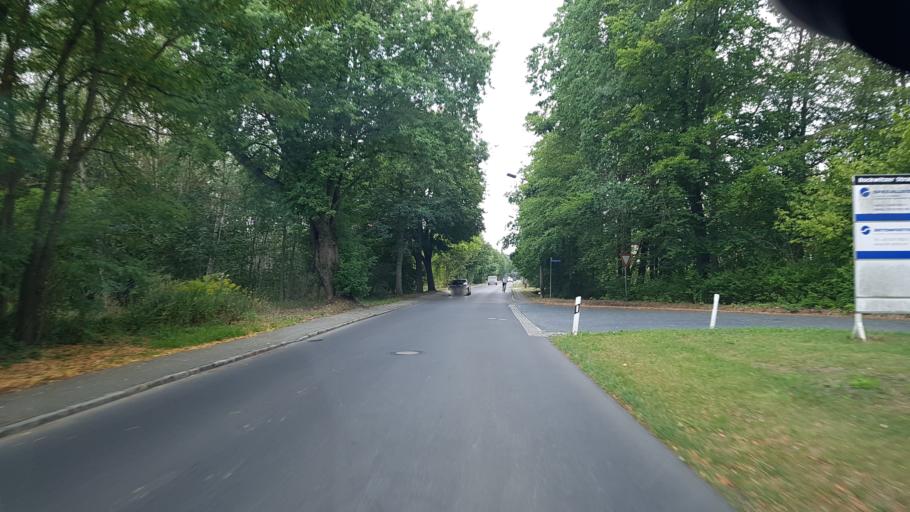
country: DE
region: Brandenburg
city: Lauchhammer
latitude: 51.4825
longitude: 13.7457
